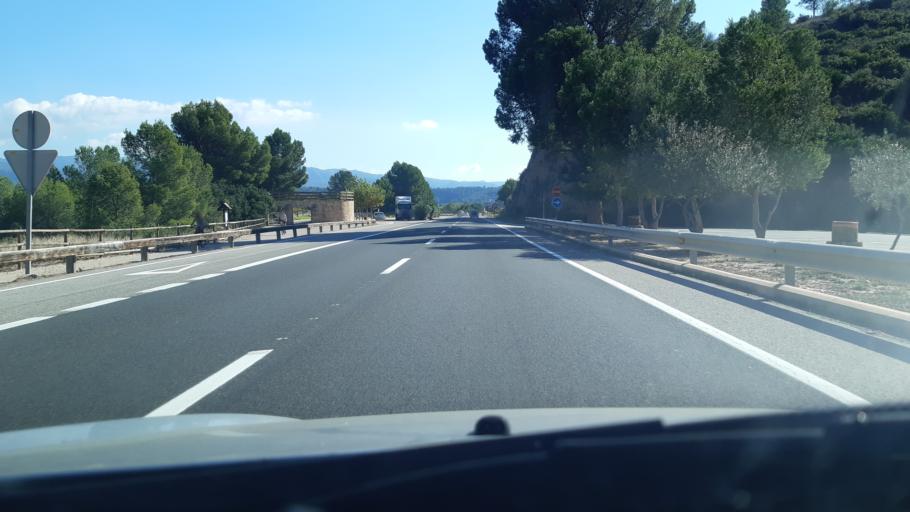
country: ES
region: Catalonia
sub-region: Provincia de Tarragona
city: Tivenys
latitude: 40.9214
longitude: 0.4909
